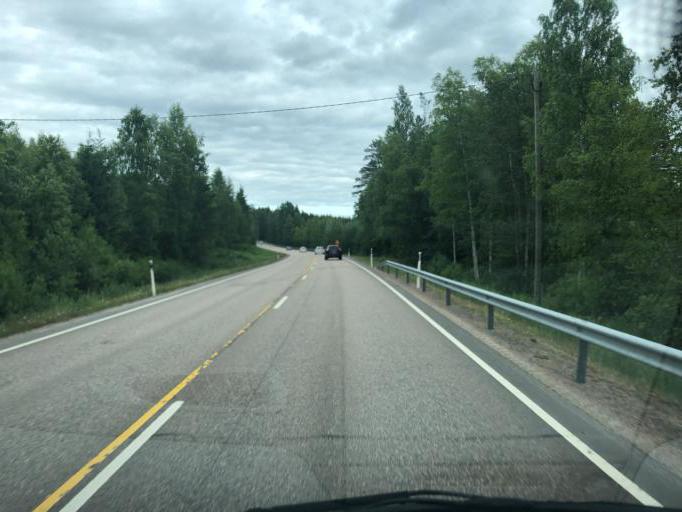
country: FI
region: Southern Savonia
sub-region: Mikkeli
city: Maentyharju
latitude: 61.1438
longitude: 27.1212
